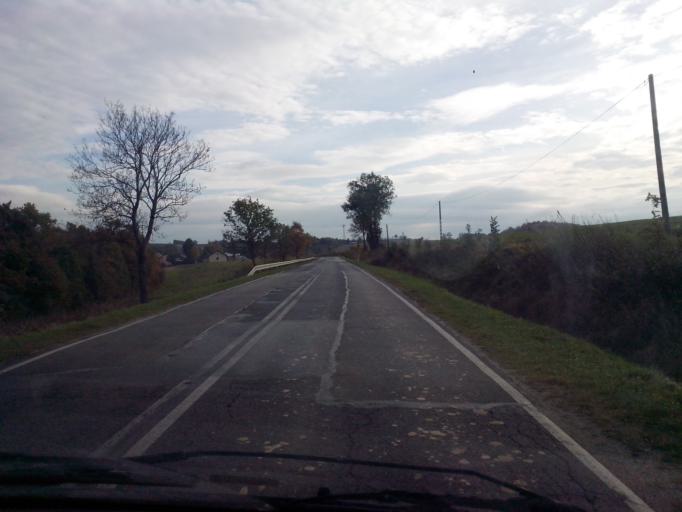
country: PL
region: Subcarpathian Voivodeship
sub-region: Powiat ropczycko-sedziszowski
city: Wielopole Skrzynskie
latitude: 49.9257
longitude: 21.6097
